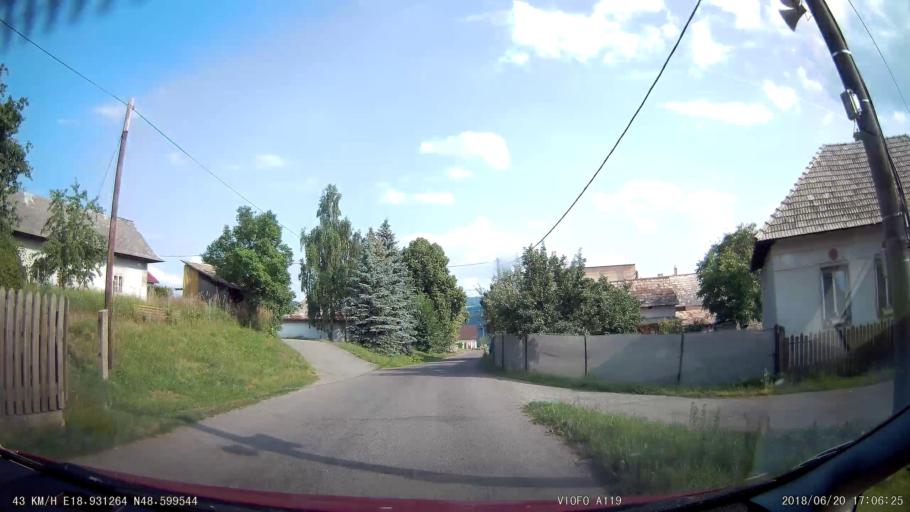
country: SK
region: Banskobystricky
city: Ziar nad Hronom
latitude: 48.5995
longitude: 18.9313
